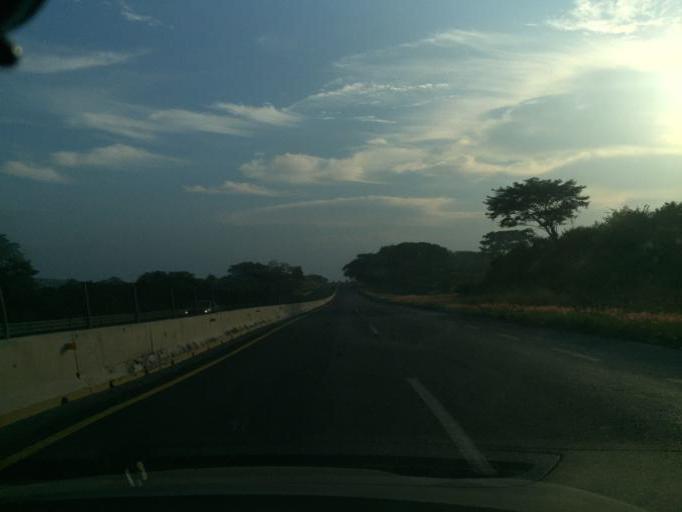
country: MX
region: Veracruz
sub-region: Tierra Blanca
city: Huixcolotla
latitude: 18.7849
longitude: -96.5334
